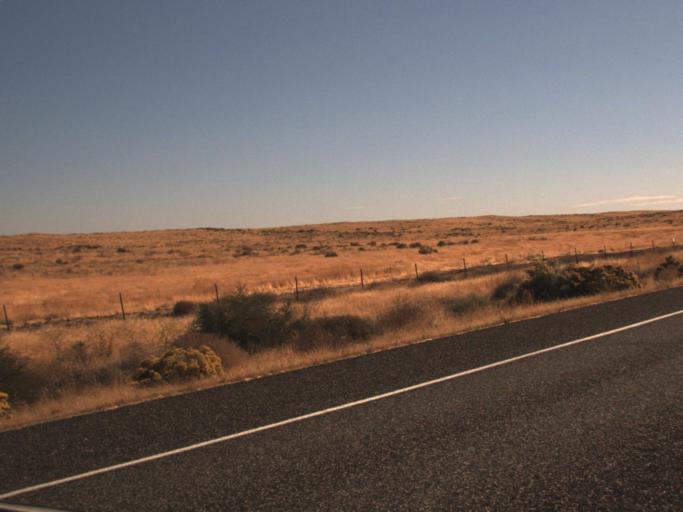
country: US
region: Washington
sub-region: Benton County
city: Benton City
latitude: 46.4581
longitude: -119.5226
